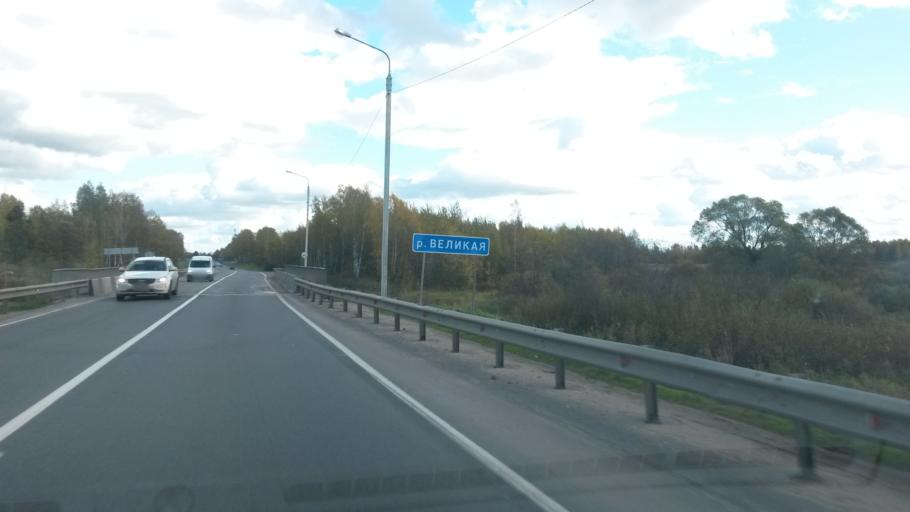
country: RU
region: Jaroslavl
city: Tunoshna
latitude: 57.5379
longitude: 40.0102
